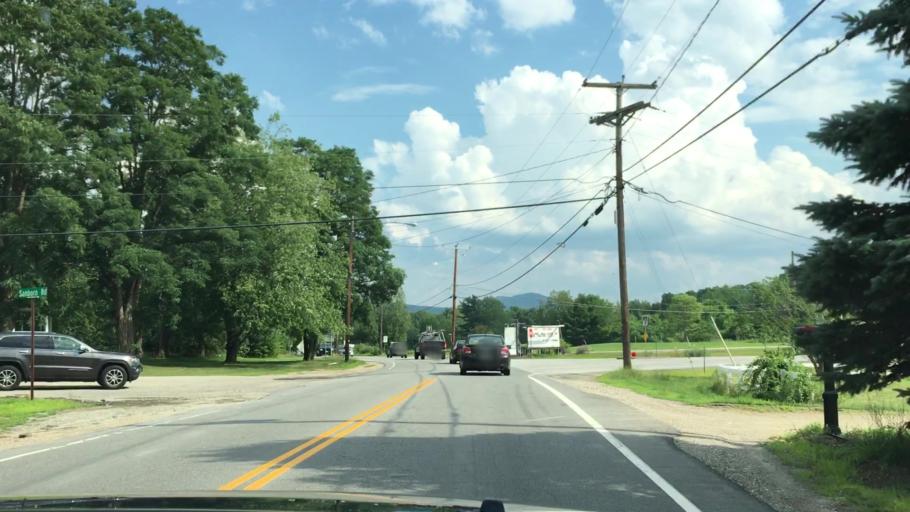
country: US
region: New Hampshire
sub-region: Belknap County
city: Gilford
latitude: 43.5890
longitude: -71.4216
